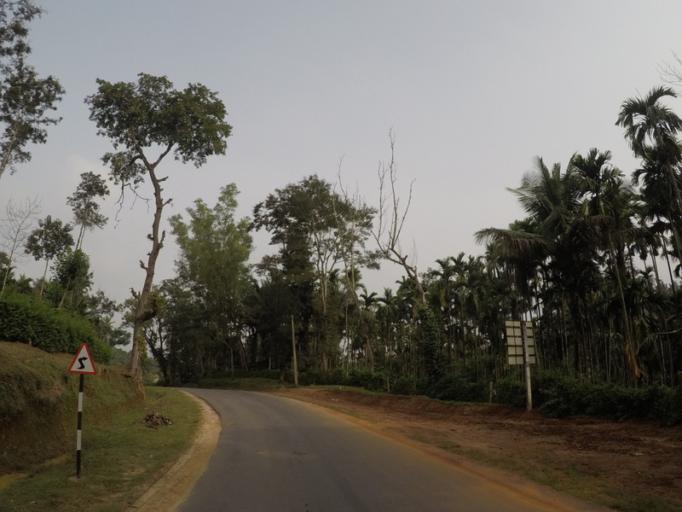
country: IN
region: Karnataka
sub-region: Chikmagalur
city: Chikmagalur
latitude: 13.3342
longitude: 75.5540
